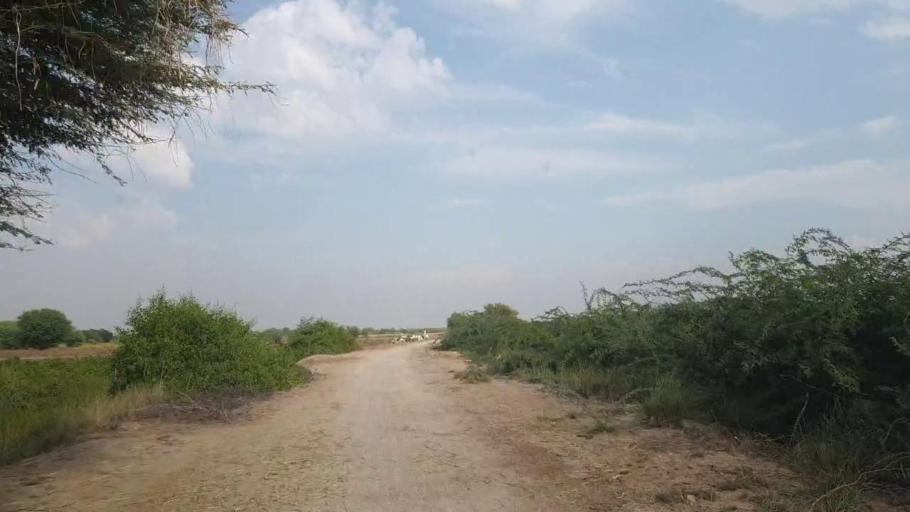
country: PK
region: Sindh
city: Digri
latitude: 25.0111
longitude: 69.0631
